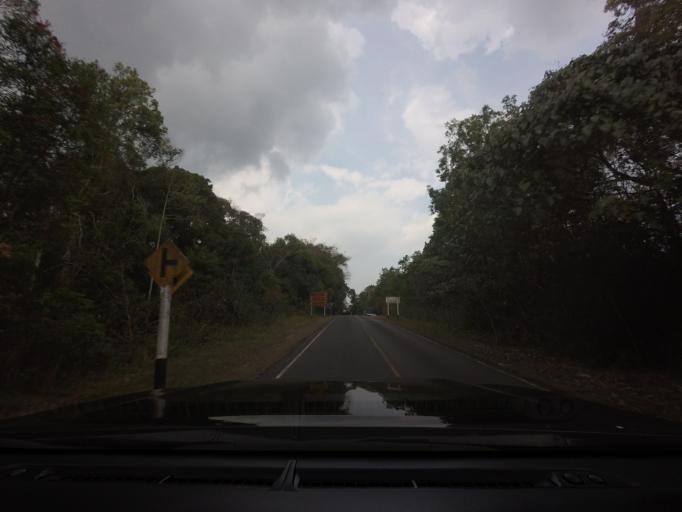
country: TH
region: Nakhon Nayok
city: Nakhon Nayok
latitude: 14.4052
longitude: 101.3688
